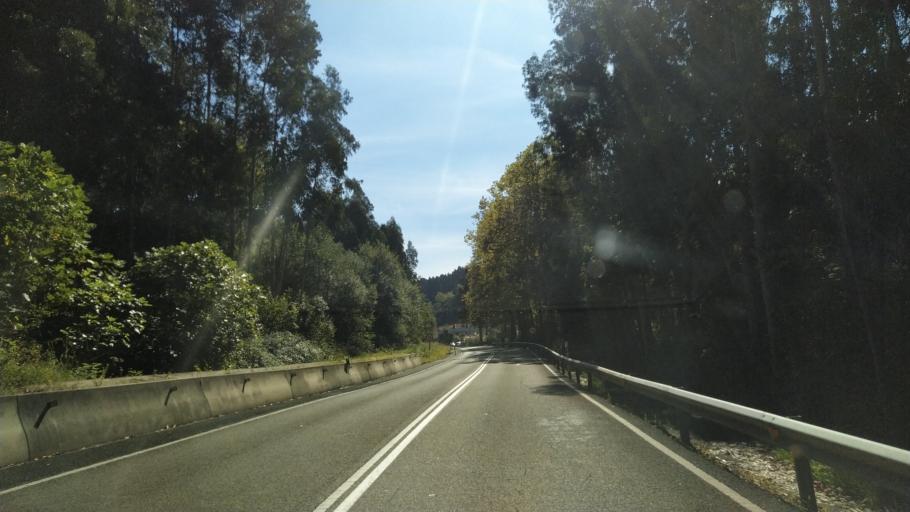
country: ES
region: Cantabria
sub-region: Provincia de Cantabria
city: Liendo
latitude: 43.3840
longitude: -3.3183
